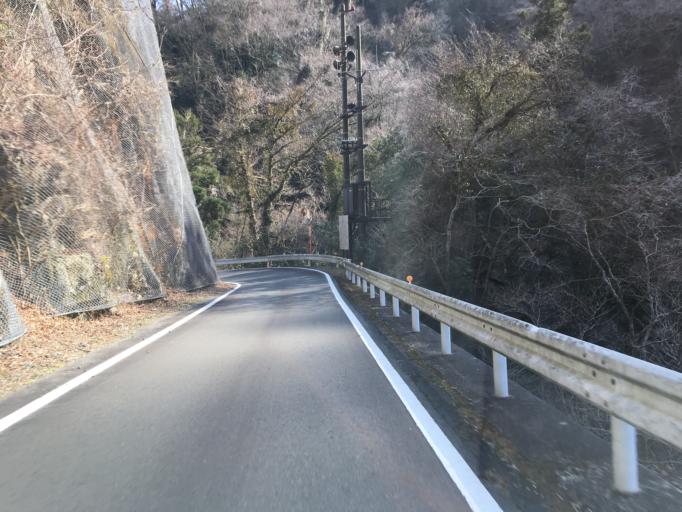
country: JP
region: Ibaraki
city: Kitaibaraki
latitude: 36.7844
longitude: 140.6743
